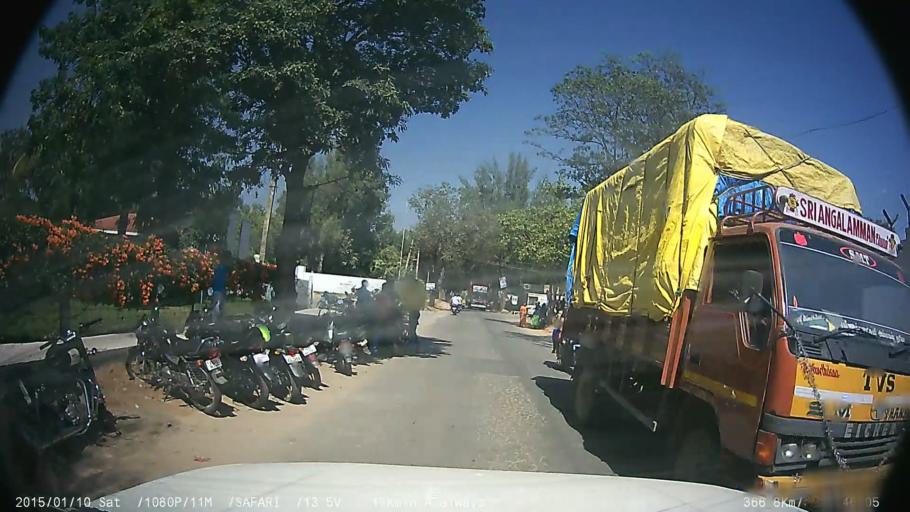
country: IN
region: Tamil Nadu
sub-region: Krishnagiri
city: Hosur
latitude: 12.7673
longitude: 77.7965
